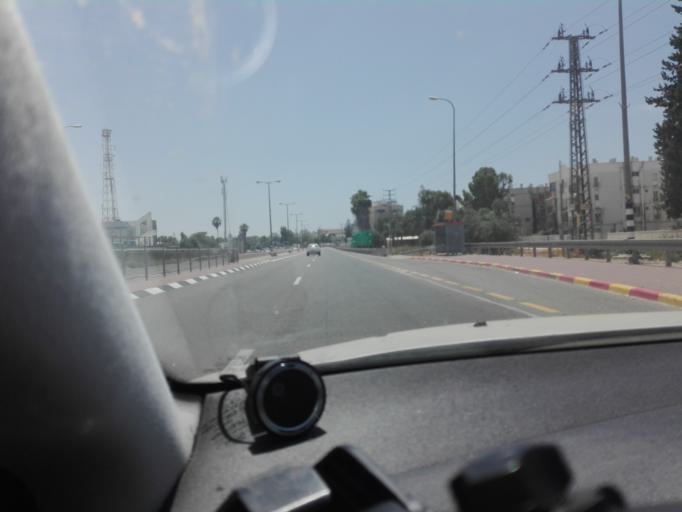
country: IL
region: Central District
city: Bene 'Ayish
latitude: 31.7302
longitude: 34.7531
